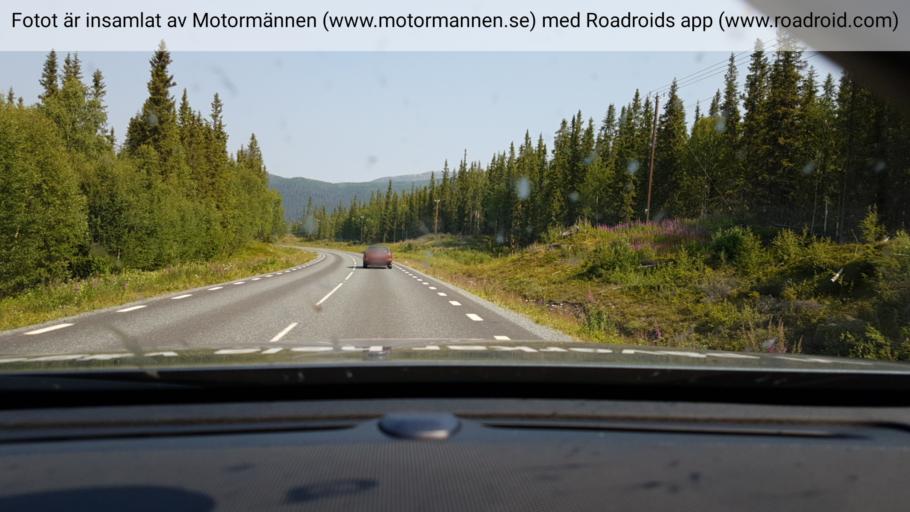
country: SE
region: Vaesterbotten
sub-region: Vilhelmina Kommun
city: Sjoberg
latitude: 65.6155
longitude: 15.5344
